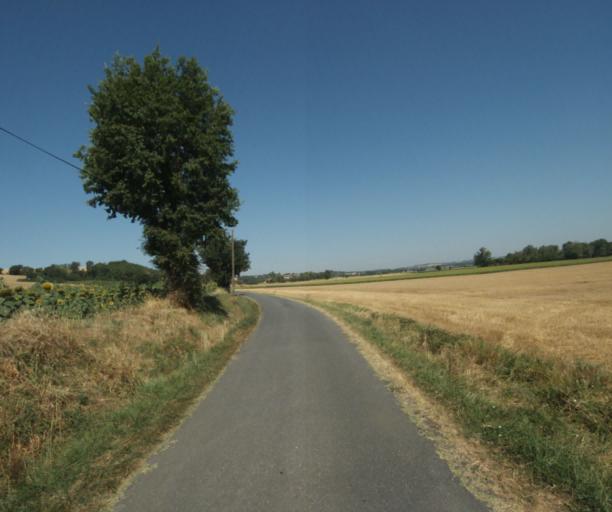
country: FR
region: Midi-Pyrenees
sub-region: Departement de la Haute-Garonne
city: Revel
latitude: 43.5136
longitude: 1.9499
